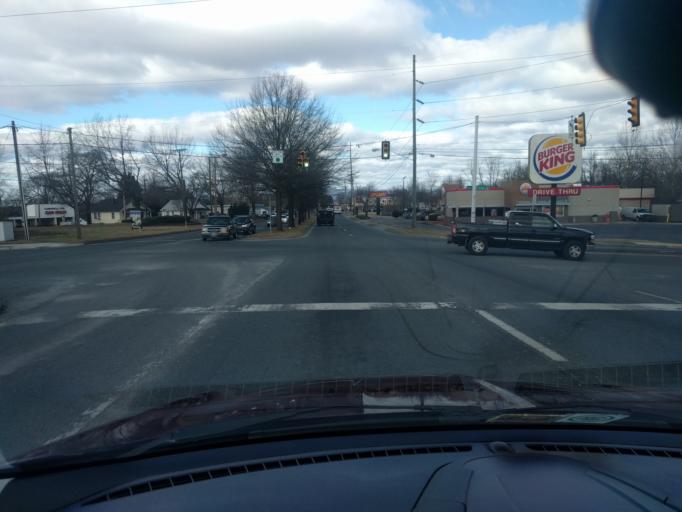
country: US
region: Virginia
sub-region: City of Lynchburg
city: Lynchburg
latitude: 37.3804
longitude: -79.1335
